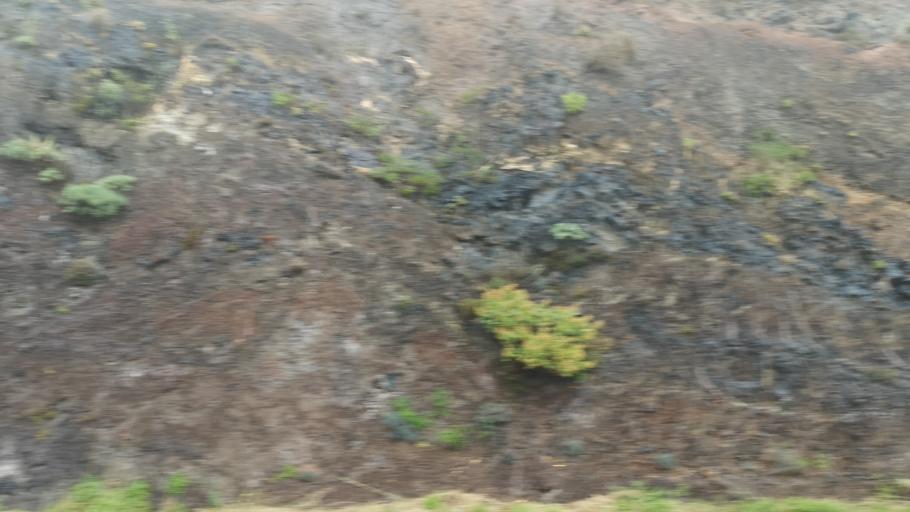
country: ES
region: Canary Islands
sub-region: Provincia de Santa Cruz de Tenerife
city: Alajero
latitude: 28.0942
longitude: -17.1914
